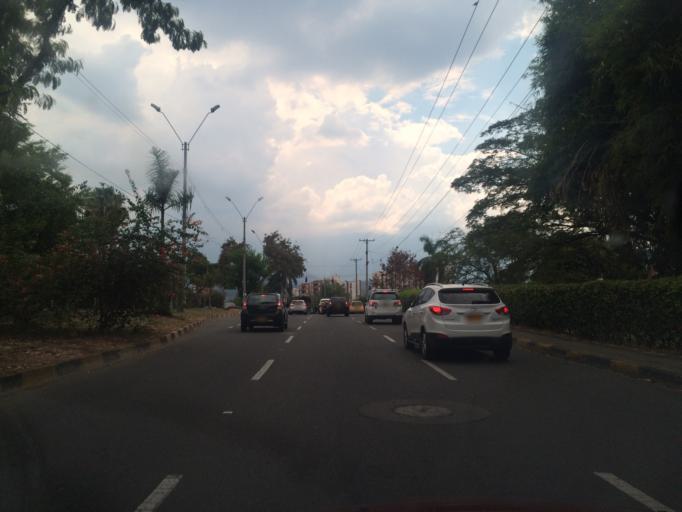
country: CO
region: Valle del Cauca
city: Cali
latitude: 3.3877
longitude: -76.5315
